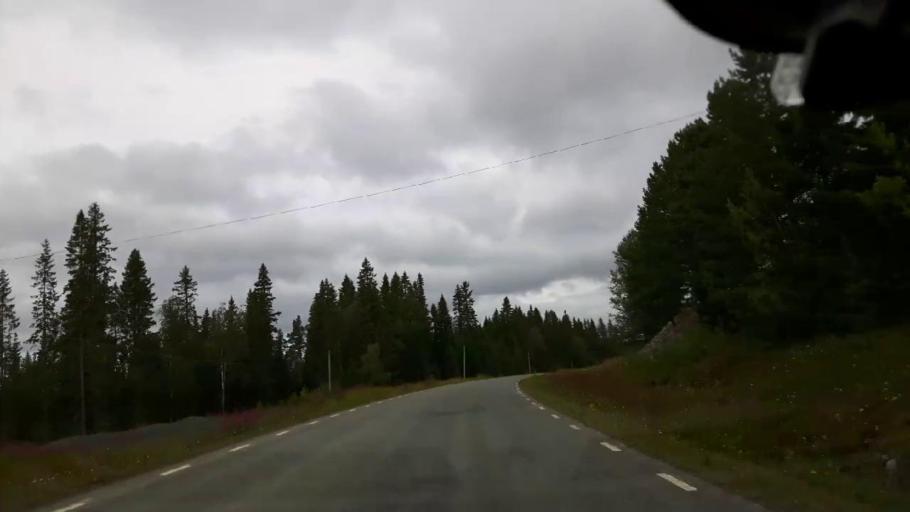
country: SE
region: Jaemtland
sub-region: Krokoms Kommun
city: Valla
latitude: 63.5138
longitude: 13.8789
